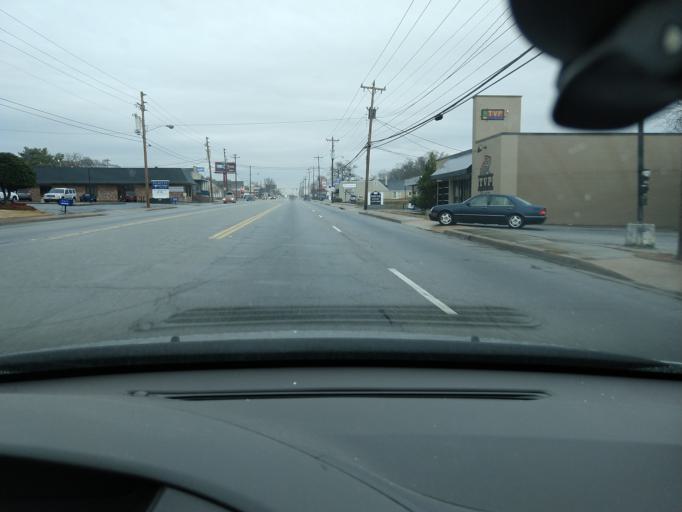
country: US
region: South Carolina
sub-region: Greenville County
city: Greenville
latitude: 34.8466
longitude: -82.3685
